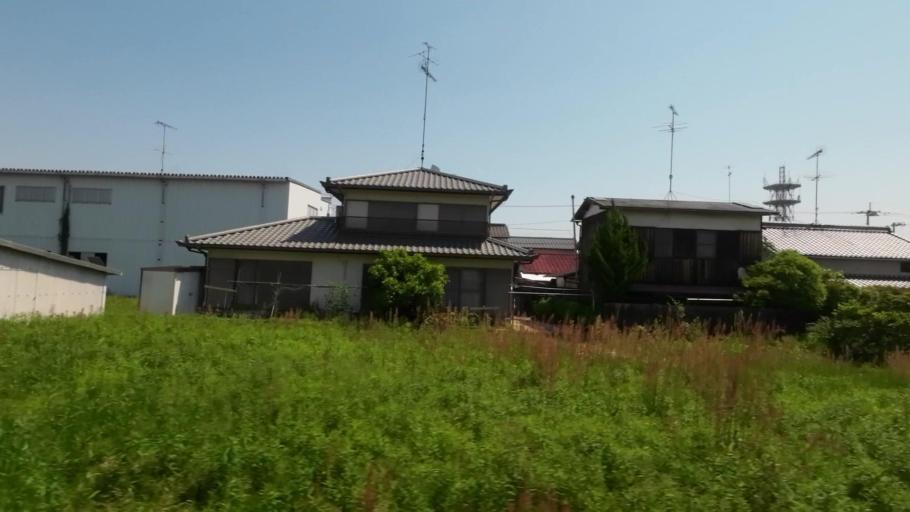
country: JP
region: Ehime
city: Saijo
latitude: 33.9345
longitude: 133.0813
